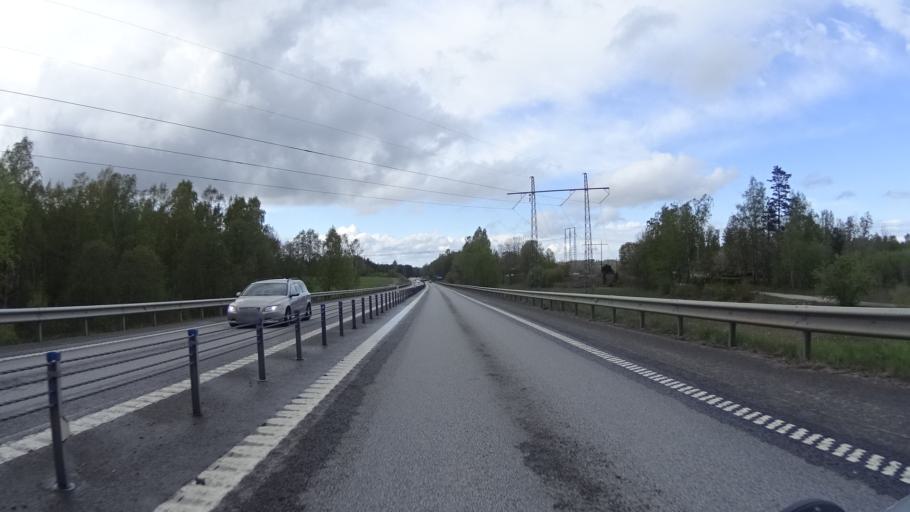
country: SE
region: OErebro
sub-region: Askersunds Kommun
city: Asbro
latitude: 59.0508
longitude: 15.0153
